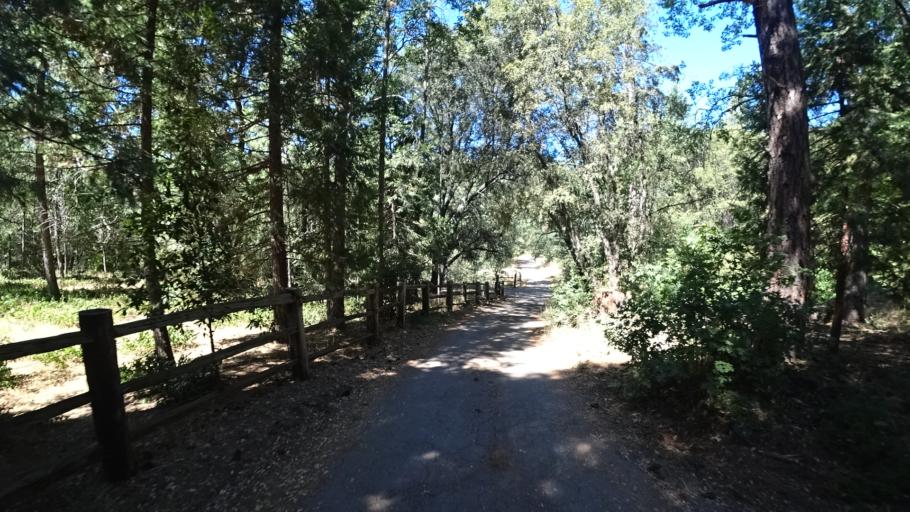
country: US
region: California
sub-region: Calaveras County
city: Forest Meadows
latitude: 38.1737
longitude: -120.3728
